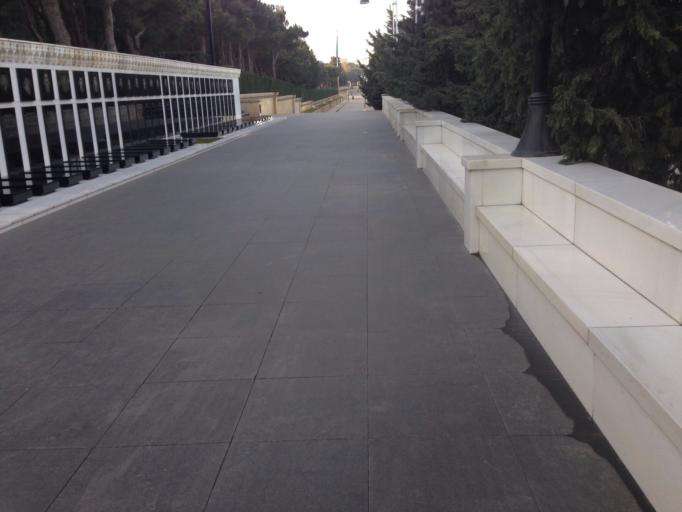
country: AZ
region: Baki
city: Badamdar
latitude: 40.3565
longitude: 49.8286
